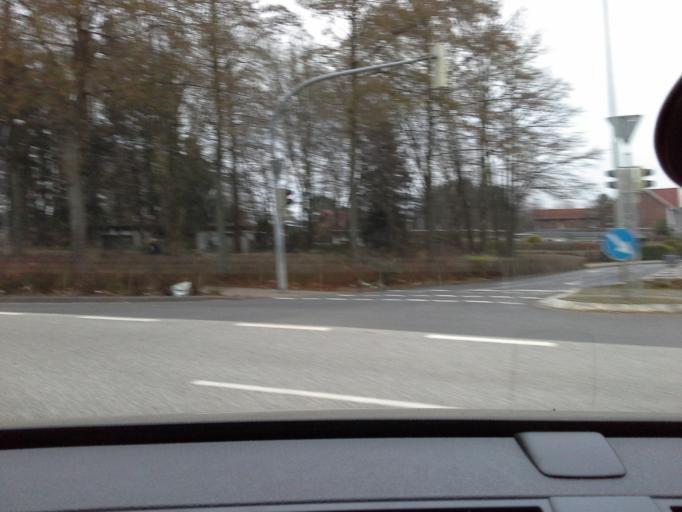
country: DE
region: Schleswig-Holstein
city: Quickborn
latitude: 53.7220
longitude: 9.9022
